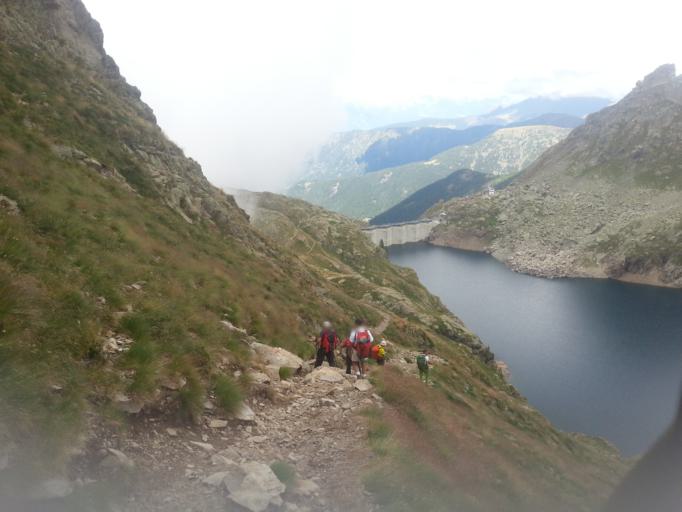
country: IT
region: Lombardy
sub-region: Provincia di Bergamo
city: Valtorta
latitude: 46.0217
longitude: 9.5222
